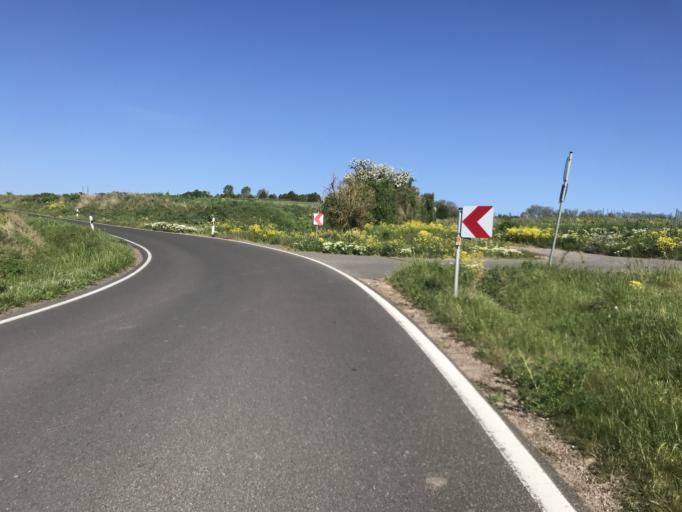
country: DE
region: Rheinland-Pfalz
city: Zornheim
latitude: 49.8723
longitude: 8.2198
